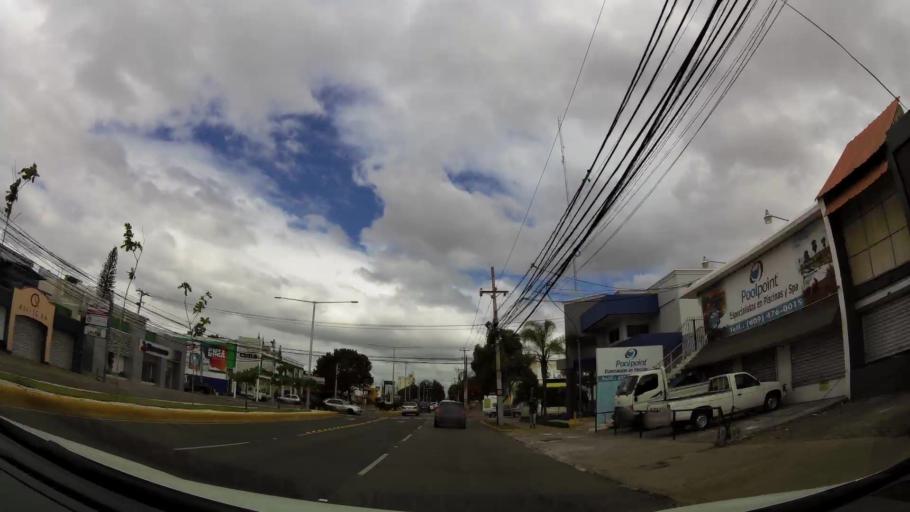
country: DO
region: Nacional
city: Bella Vista
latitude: 18.4728
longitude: -69.9607
